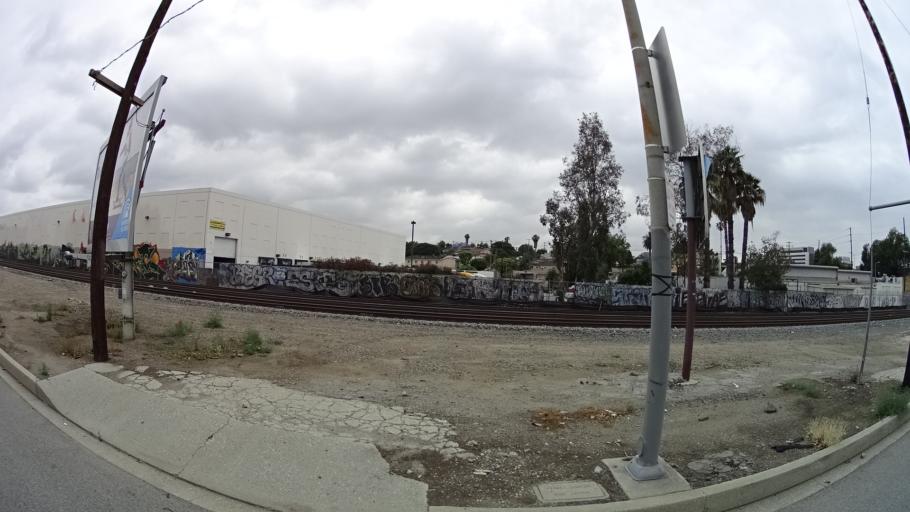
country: US
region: California
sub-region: Los Angeles County
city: Boyle Heights
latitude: 34.0644
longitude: -118.1958
